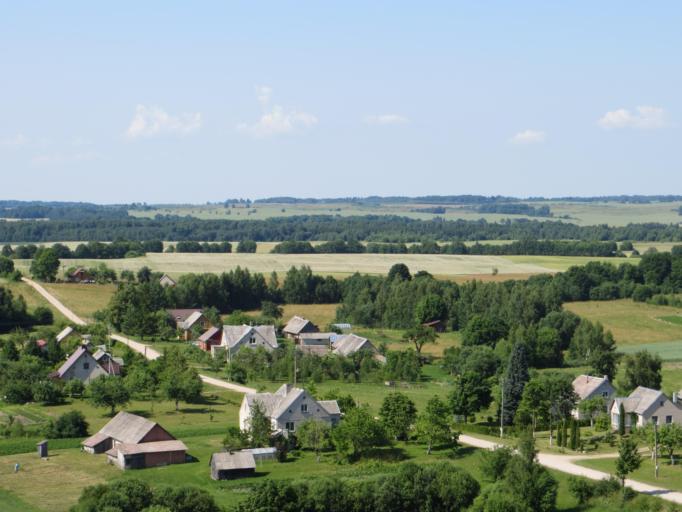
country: LT
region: Utenos apskritis
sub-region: Anyksciai
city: Anyksciai
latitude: 55.2871
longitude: 25.0690
